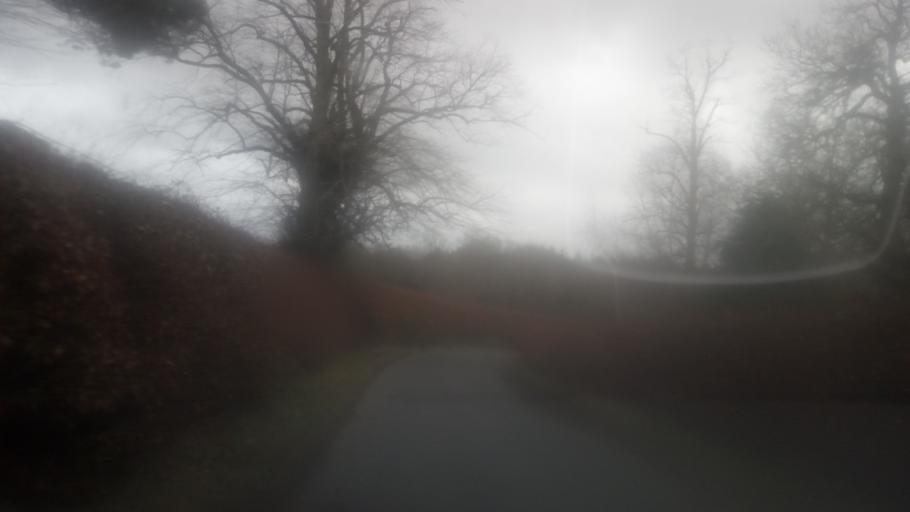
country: GB
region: Scotland
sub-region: The Scottish Borders
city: Jedburgh
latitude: 55.4795
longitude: -2.5258
